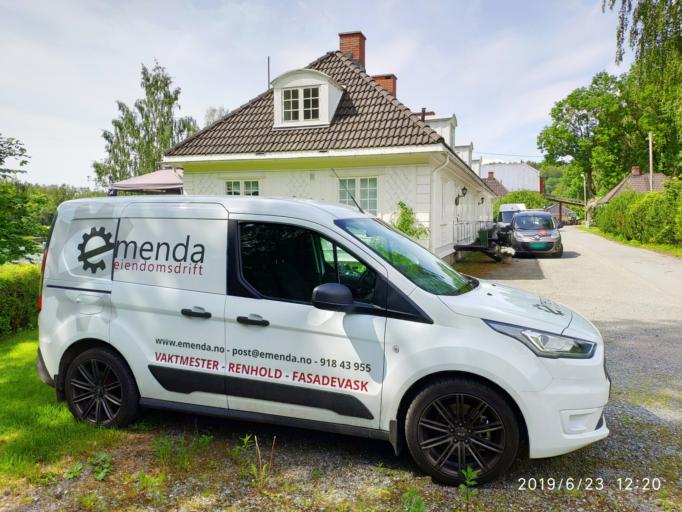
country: NO
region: Oppland
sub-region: Jevnaker
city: Jevnaker
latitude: 60.2003
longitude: 10.3346
